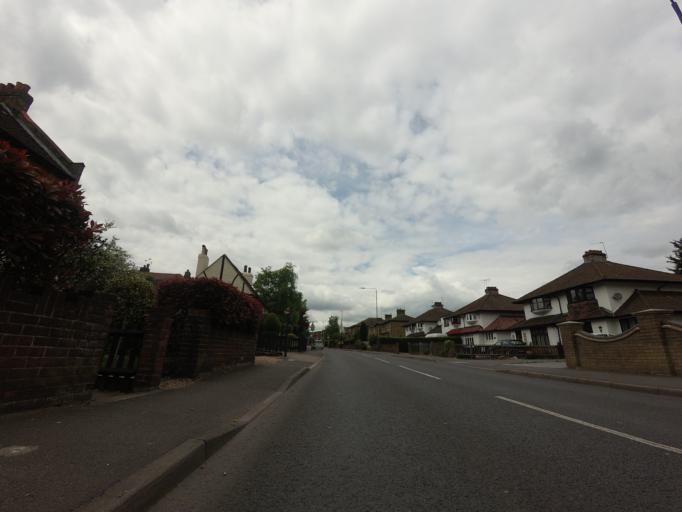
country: GB
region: England
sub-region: Greater London
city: Sidcup
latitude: 51.4195
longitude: 0.1164
